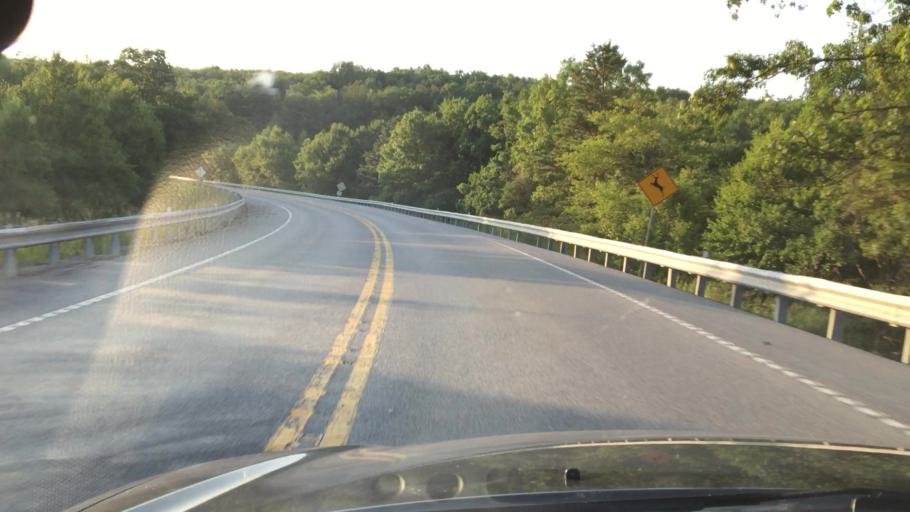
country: US
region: Pennsylvania
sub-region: Carbon County
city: Nesquehoning
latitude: 40.8775
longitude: -75.7853
